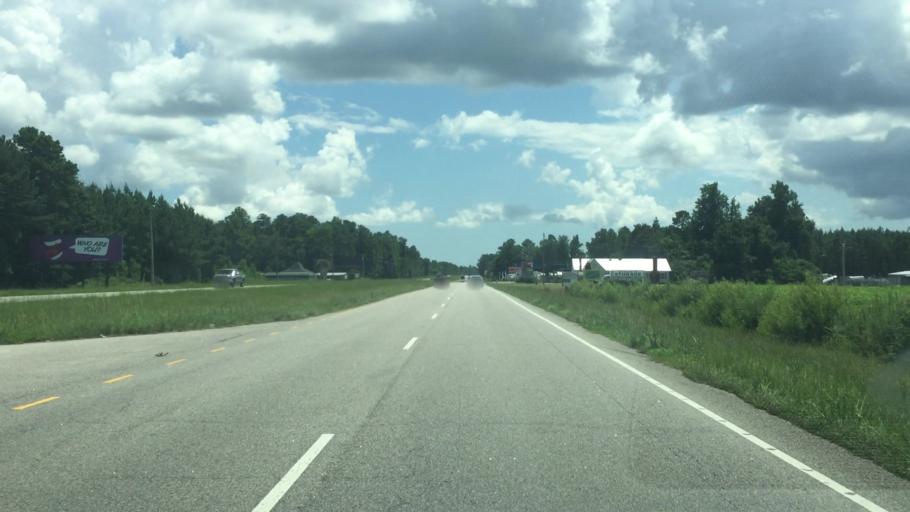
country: US
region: South Carolina
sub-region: Horry County
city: Loris
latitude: 33.9855
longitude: -78.7467
